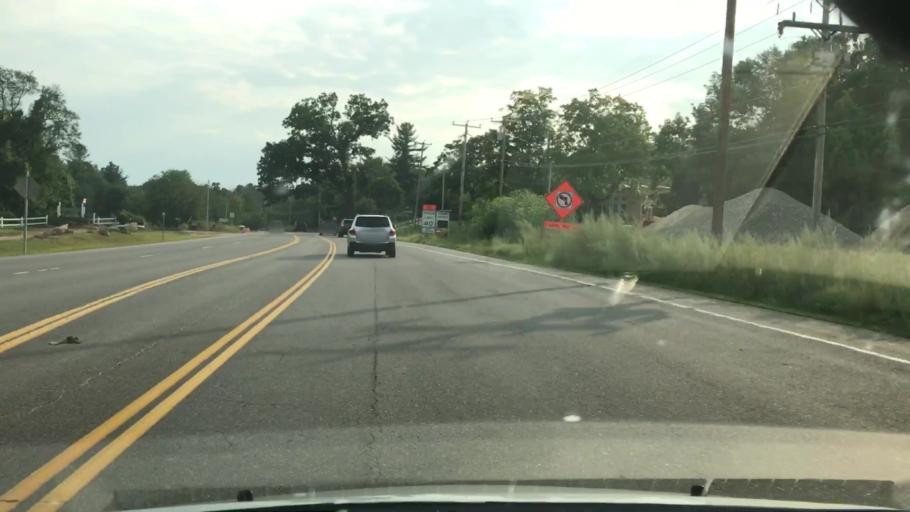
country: US
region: New Hampshire
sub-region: Hillsborough County
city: Bedford
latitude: 42.9569
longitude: -71.5068
